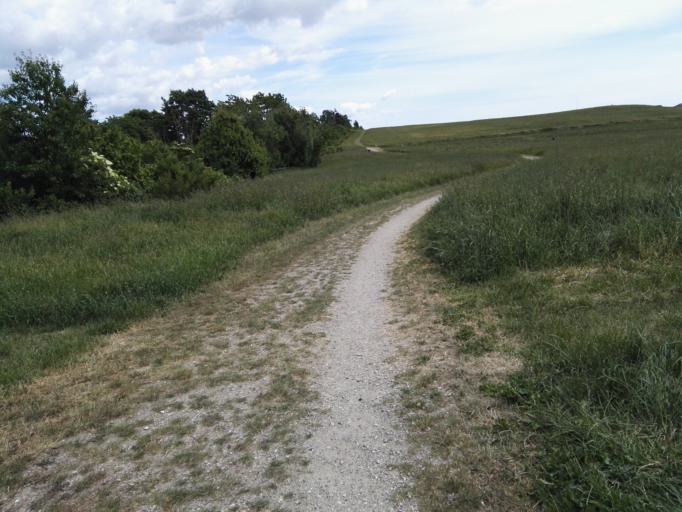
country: DK
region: Capital Region
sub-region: Egedal Kommune
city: Stenlose
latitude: 55.7639
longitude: 12.1808
